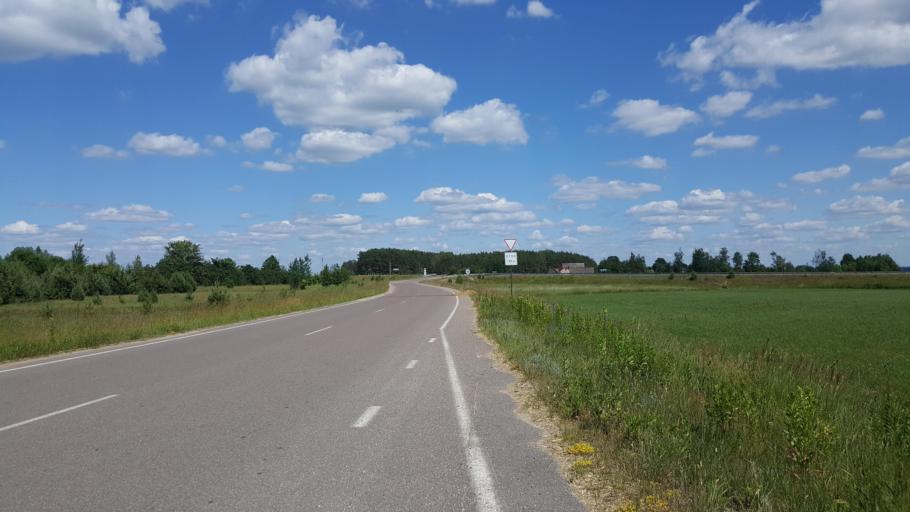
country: PL
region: Podlasie
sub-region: Powiat hajnowski
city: Czeremcha
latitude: 52.5395
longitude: 23.5303
